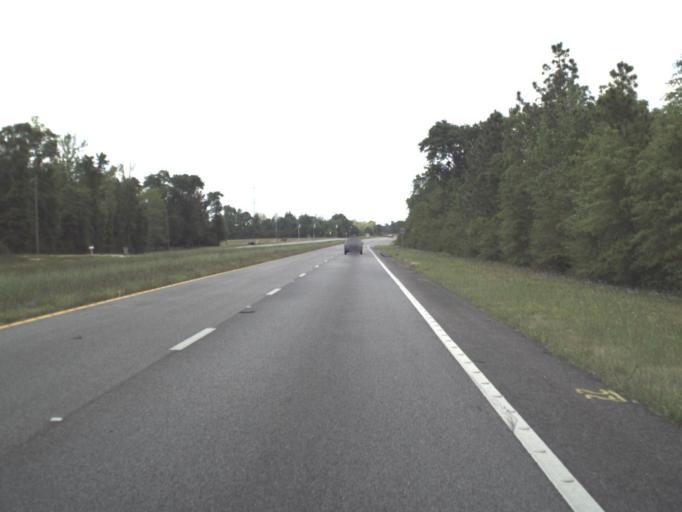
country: US
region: Florida
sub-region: Escambia County
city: Molino
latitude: 30.7361
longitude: -87.3489
